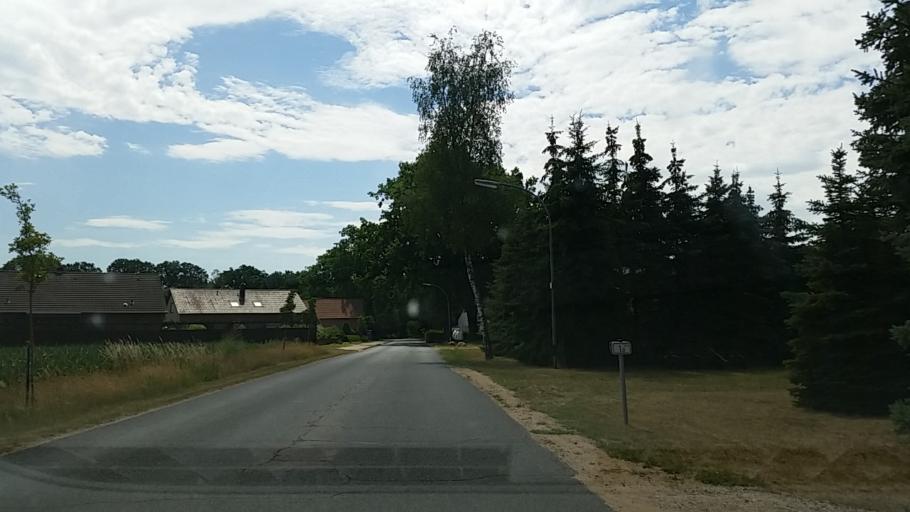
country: DE
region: Lower Saxony
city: Meinersen
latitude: 52.4156
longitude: 10.3358
